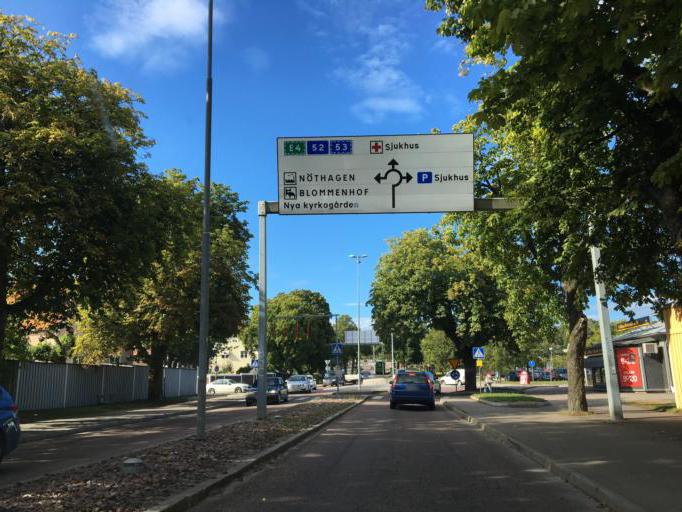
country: SE
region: Soedermanland
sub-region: Nykopings Kommun
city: Nykoping
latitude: 58.7578
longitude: 17.0001
